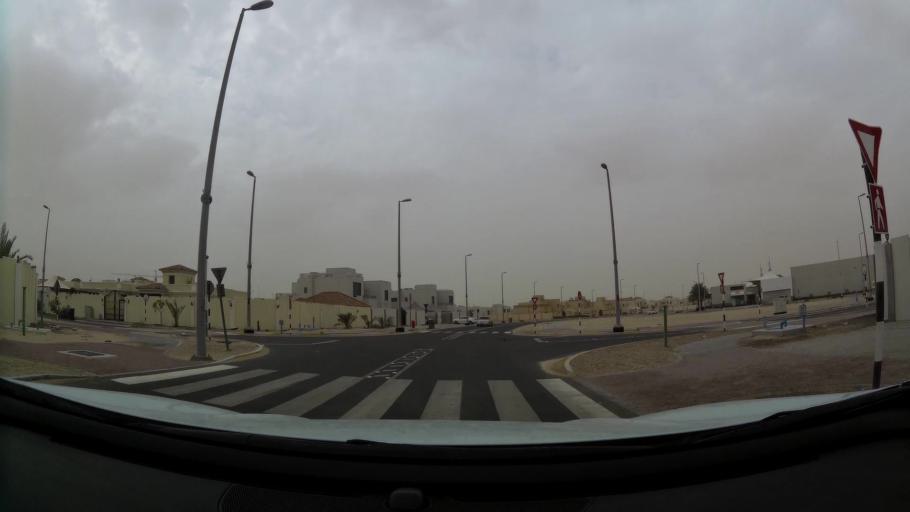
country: AE
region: Abu Dhabi
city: Abu Dhabi
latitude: 24.4349
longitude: 54.7343
